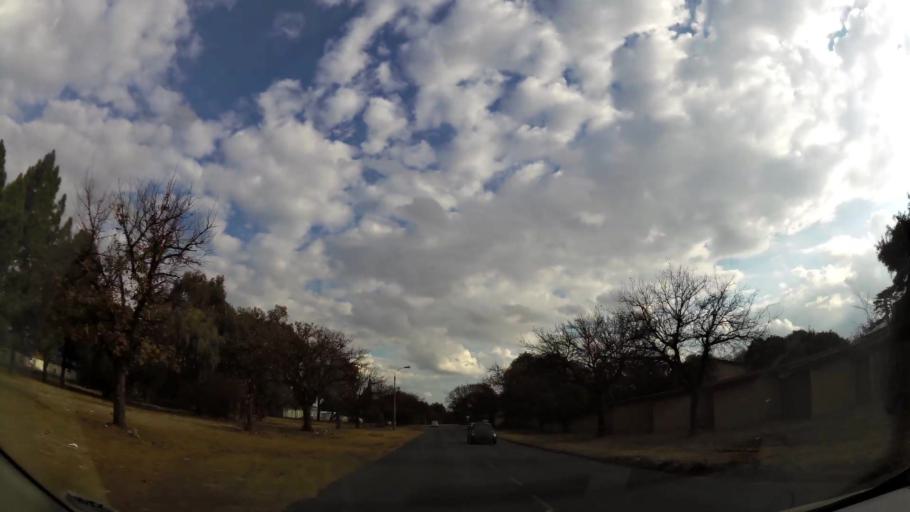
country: ZA
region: Orange Free State
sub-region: Fezile Dabi District Municipality
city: Sasolburg
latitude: -26.8231
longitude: 27.8320
